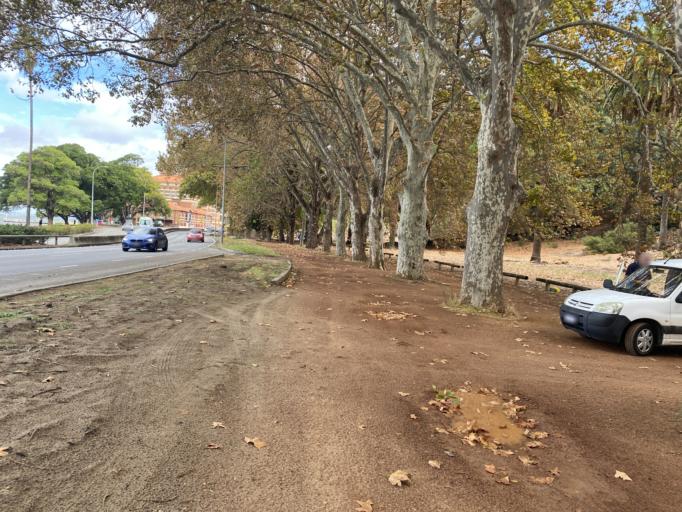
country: AU
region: Western Australia
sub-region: City of Perth
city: West Perth
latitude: -31.9630
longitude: 115.8423
